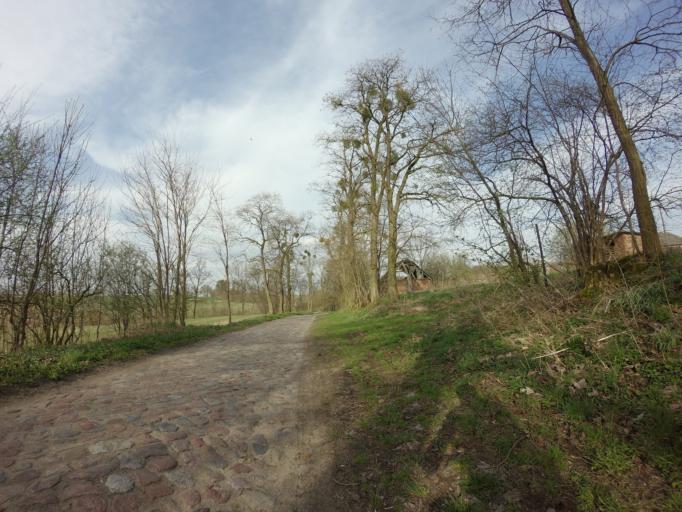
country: PL
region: West Pomeranian Voivodeship
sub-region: Powiat choszczenski
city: Choszczno
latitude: 53.1890
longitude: 15.4717
